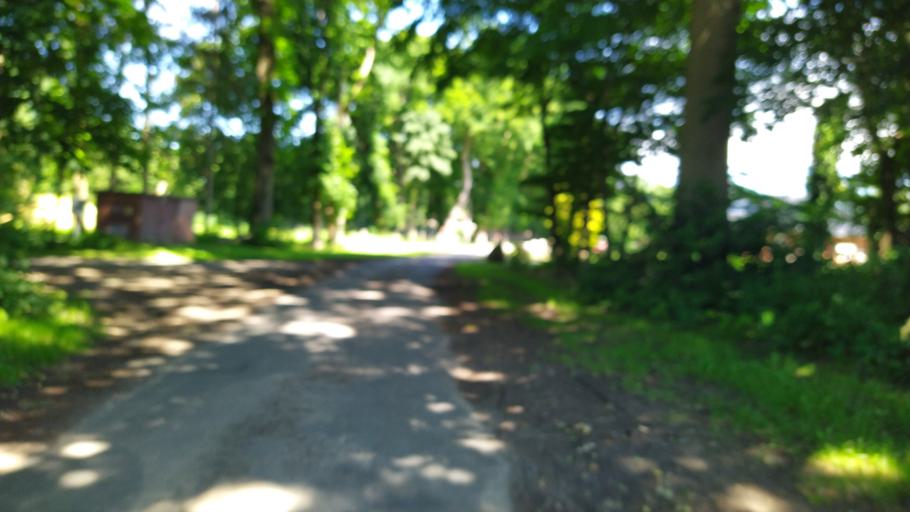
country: DE
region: Lower Saxony
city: Bargstedt
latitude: 53.4935
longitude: 9.4358
